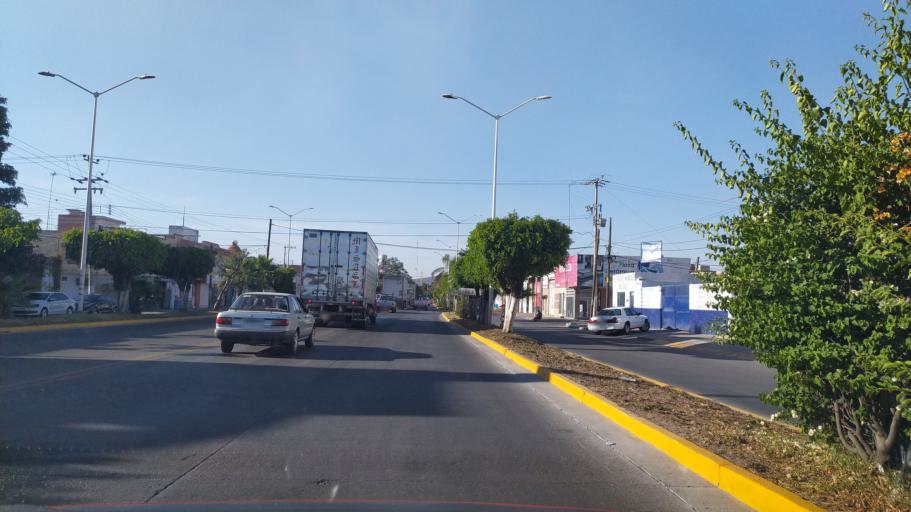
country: MX
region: Jalisco
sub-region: Poncitlan
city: Cuitzeo (La Estancia)
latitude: 20.3409
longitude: -102.7747
